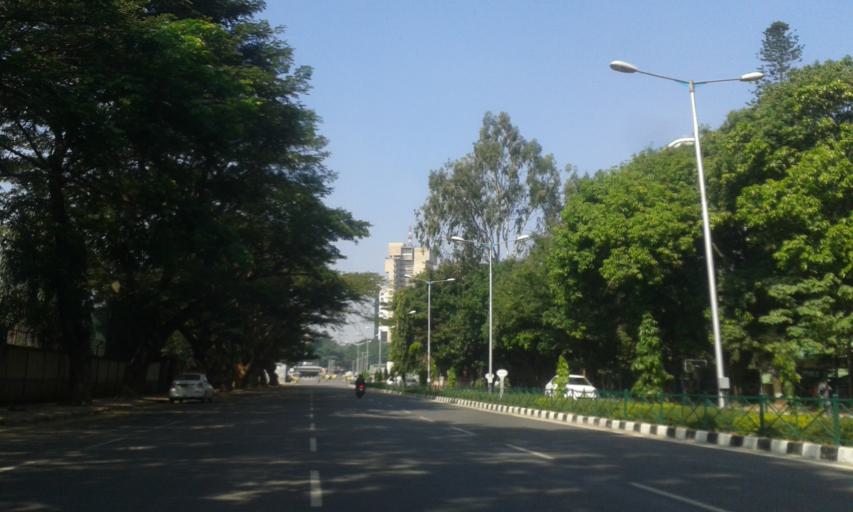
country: IN
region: Karnataka
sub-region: Bangalore Urban
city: Bangalore
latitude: 12.9799
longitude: 77.5999
